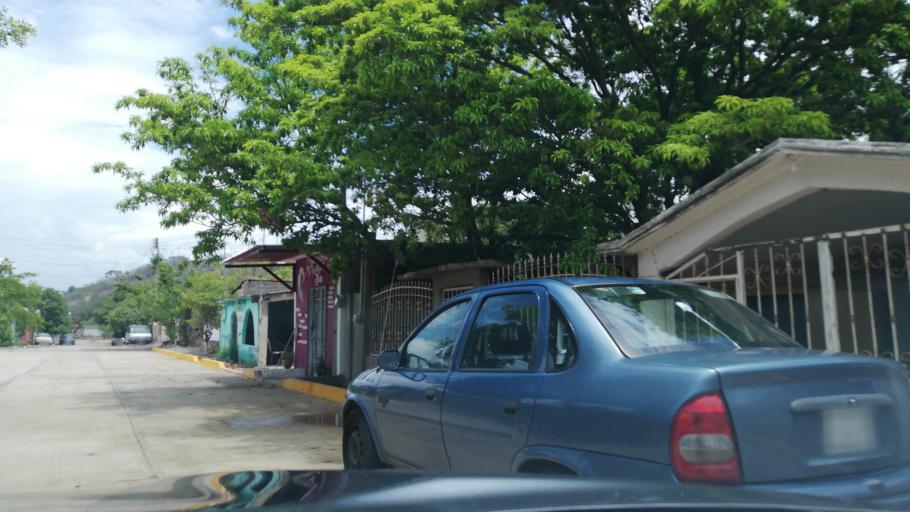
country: MX
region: Oaxaca
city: Santa Maria Jalapa del Marques
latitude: 16.4438
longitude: -95.4410
